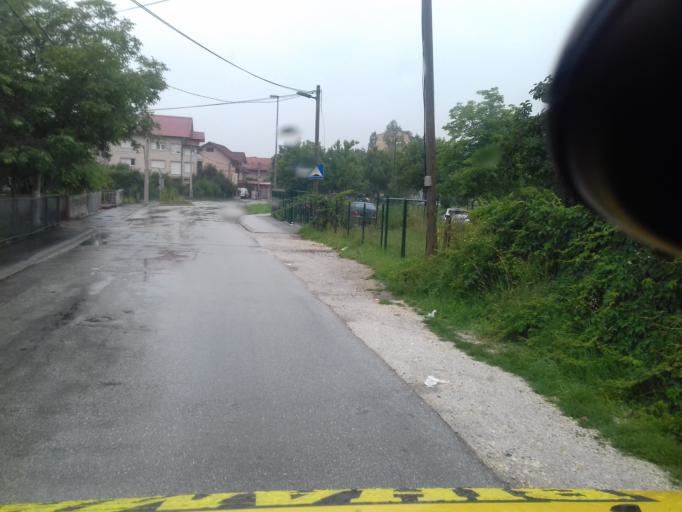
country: BA
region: Federation of Bosnia and Herzegovina
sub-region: Kanton Sarajevo
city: Sarajevo
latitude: 43.8379
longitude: 18.3406
